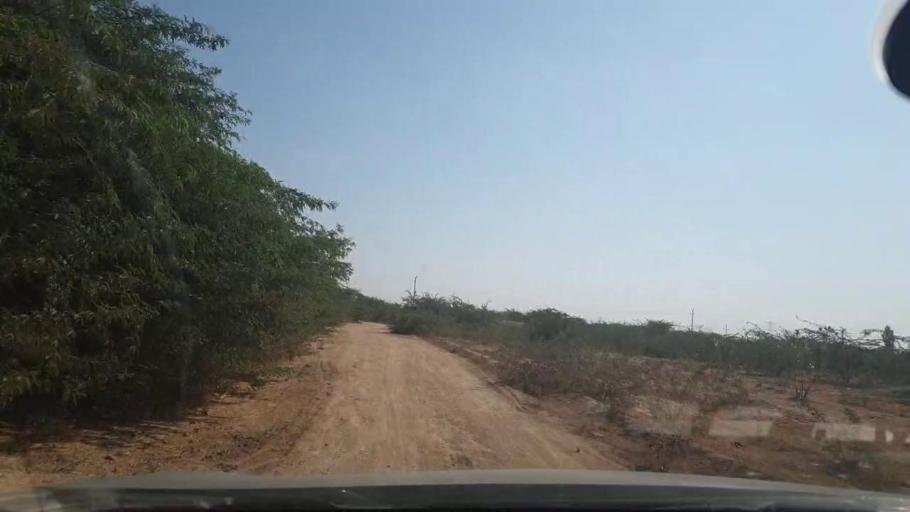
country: PK
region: Sindh
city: Malir Cantonment
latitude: 25.1694
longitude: 67.2016
